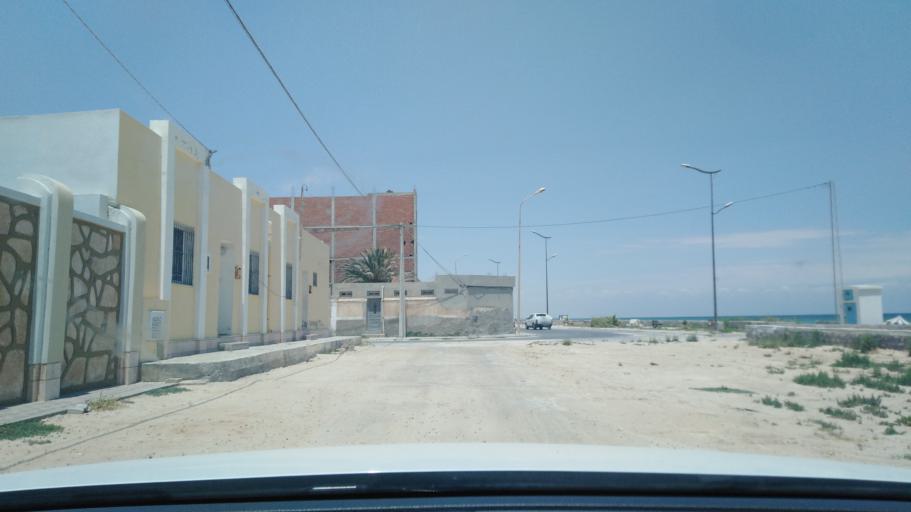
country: TN
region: Qabis
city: Gabes
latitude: 33.9518
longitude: 10.0721
